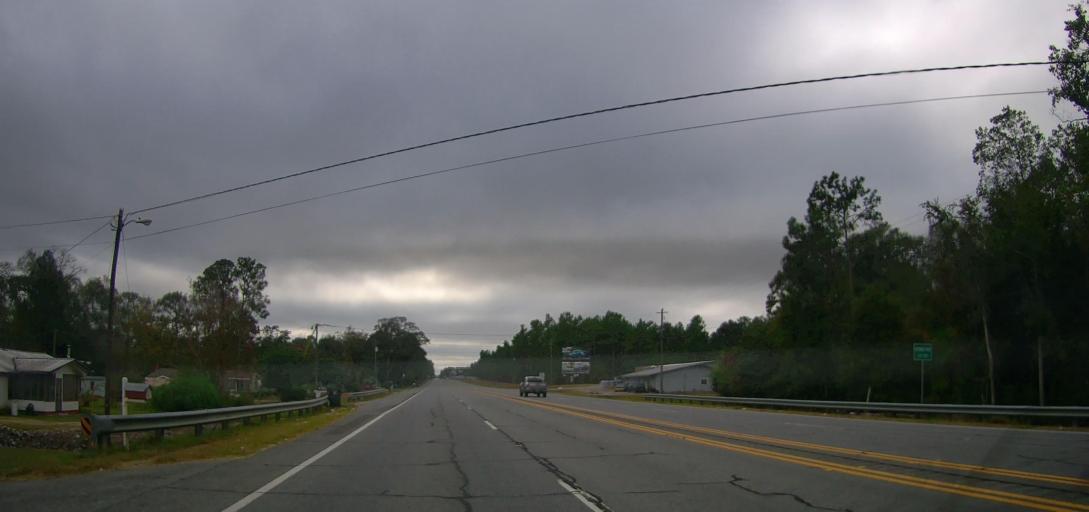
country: US
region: Georgia
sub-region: Tift County
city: Omega
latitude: 31.2839
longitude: -83.6808
